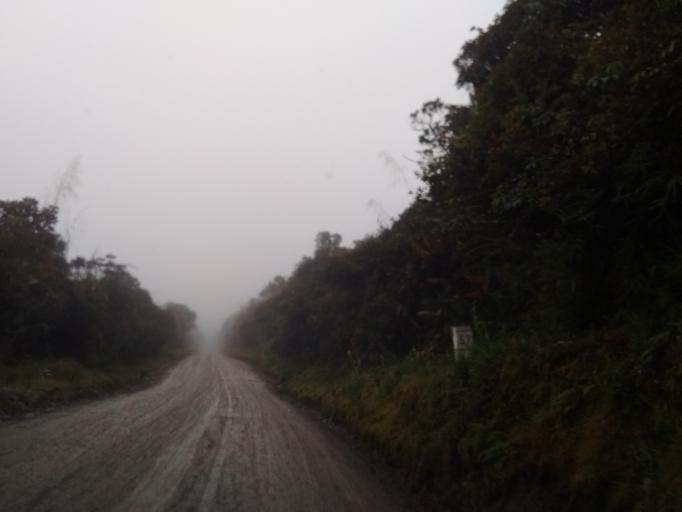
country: CO
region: Cauca
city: Paispamba
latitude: 2.1487
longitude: -76.4373
